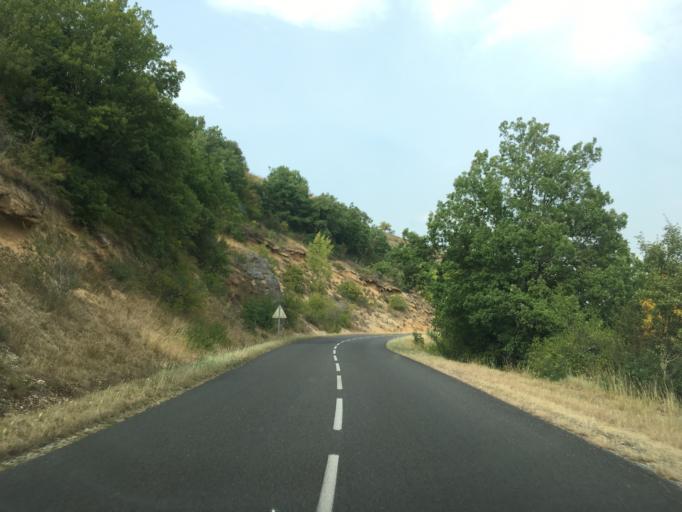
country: FR
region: Midi-Pyrenees
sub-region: Departement du Lot
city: Souillac
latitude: 44.8379
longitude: 1.5489
